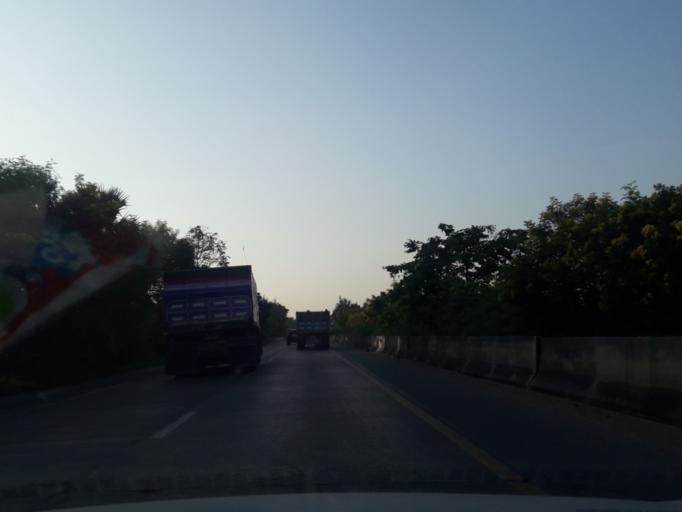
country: TH
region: Phra Nakhon Si Ayutthaya
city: Bang Pa-in
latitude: 14.1837
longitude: 100.5569
